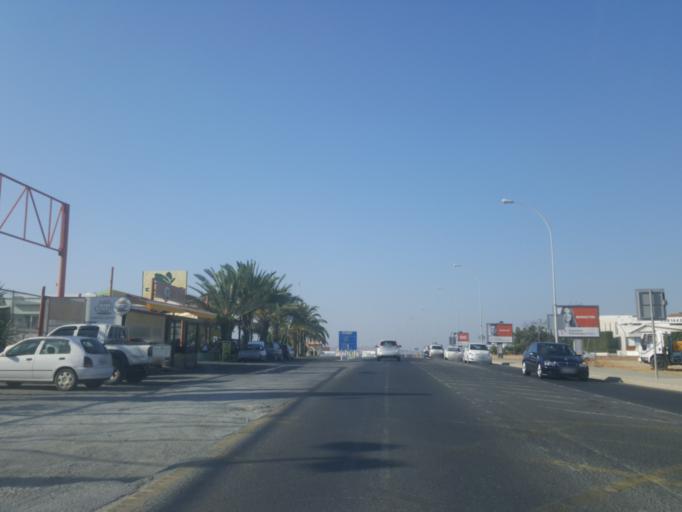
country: CY
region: Lefkosia
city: Nicosia
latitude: 35.1309
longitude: 33.3574
